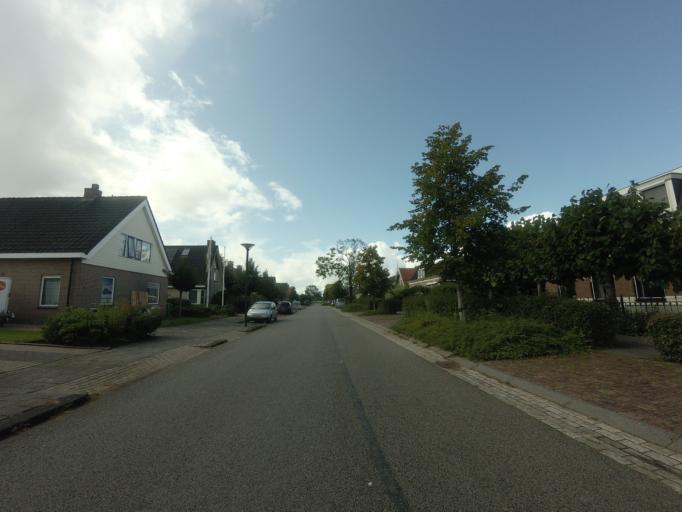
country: NL
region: Friesland
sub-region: Gemeente Leeuwarden
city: Wirdum
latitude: 53.1487
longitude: 5.7998
